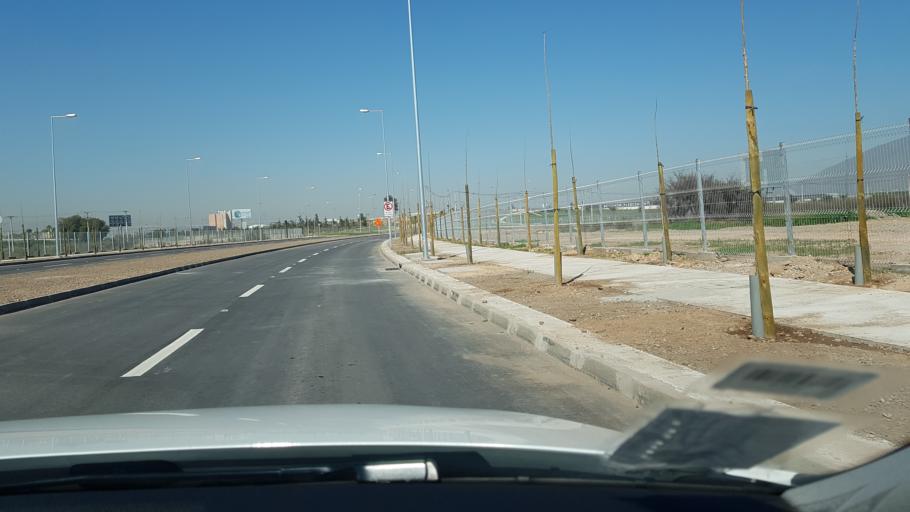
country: CL
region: Santiago Metropolitan
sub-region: Provincia de Santiago
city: Lo Prado
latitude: -33.4194
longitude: -70.7881
